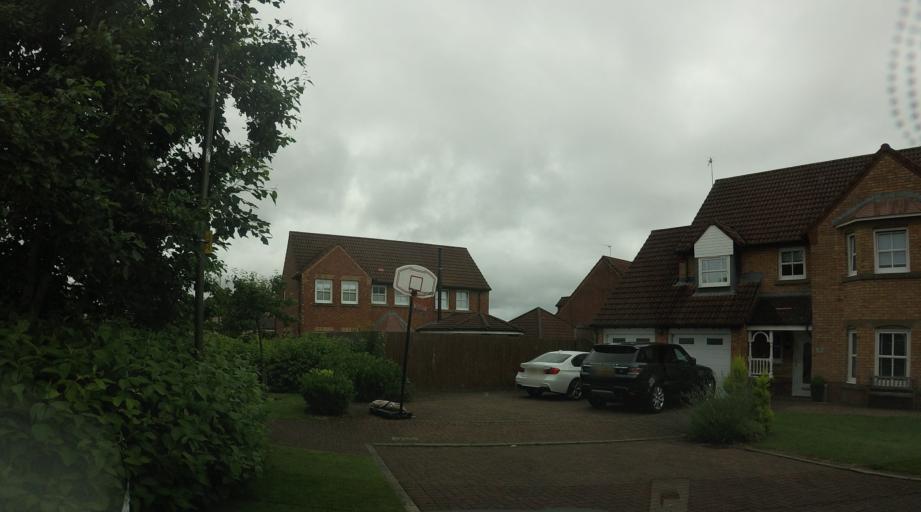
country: GB
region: Scotland
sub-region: West Lothian
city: Broxburn
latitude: 55.9296
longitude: -3.4888
